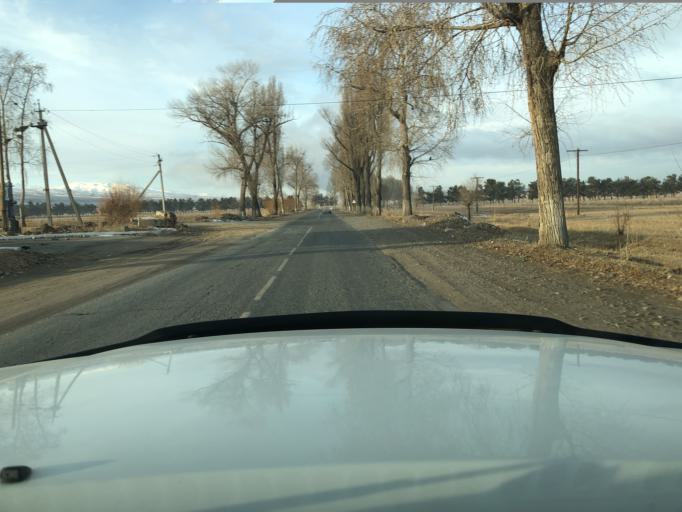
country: KG
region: Ysyk-Koel
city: Karakol
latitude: 42.4792
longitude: 78.3419
